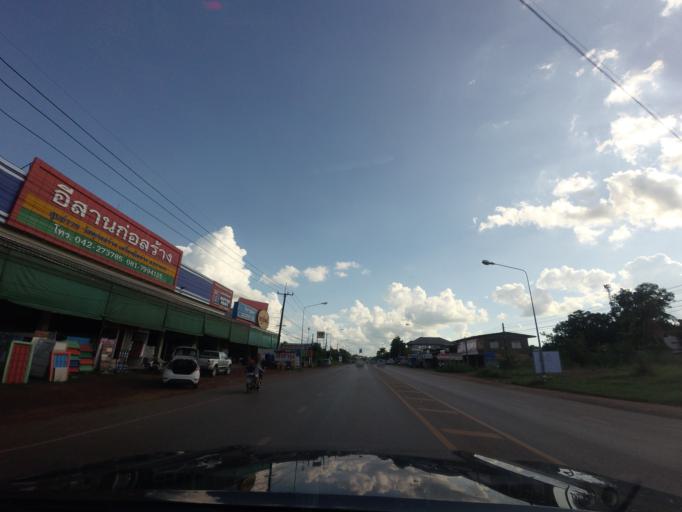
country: TH
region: Changwat Udon Thani
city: Ban Dung
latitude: 17.6832
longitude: 103.2555
